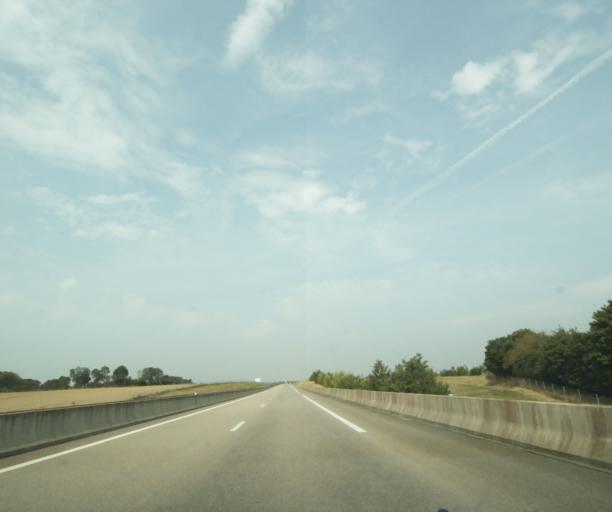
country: FR
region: Lower Normandy
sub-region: Departement du Calvados
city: Falaise
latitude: 48.8614
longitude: -0.1893
